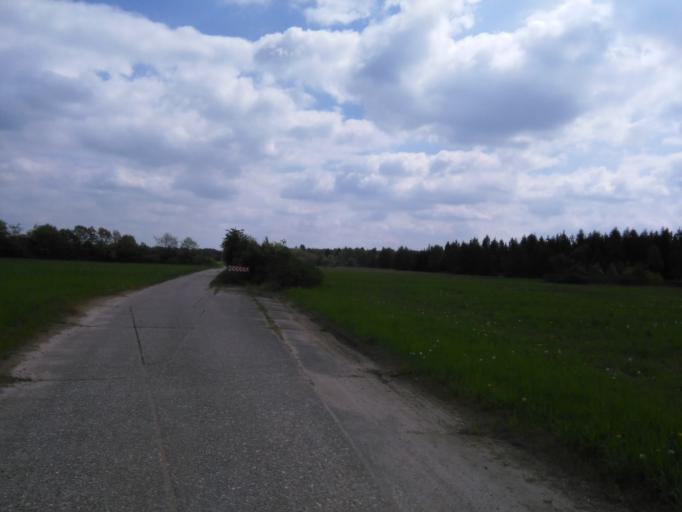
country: DK
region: Central Jutland
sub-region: Silkeborg Kommune
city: Svejbaek
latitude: 56.0532
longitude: 9.6673
